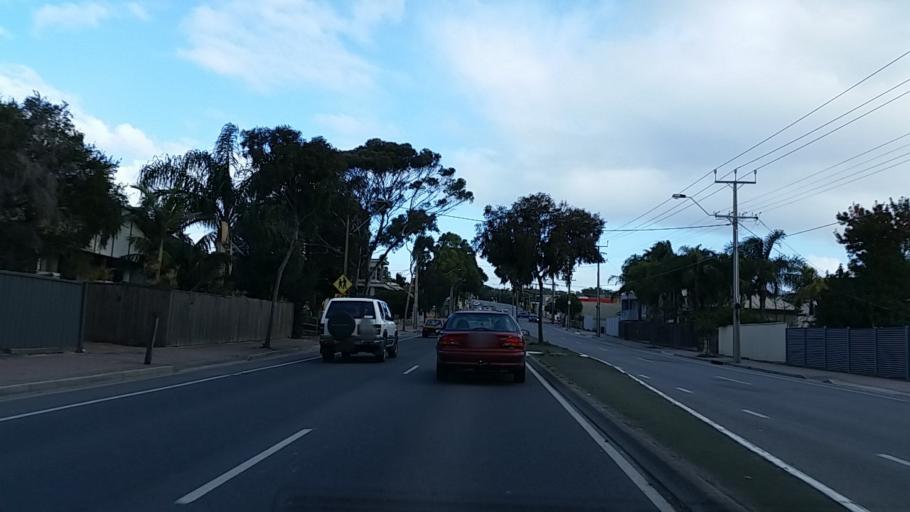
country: AU
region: South Australia
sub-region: Adelaide Hills
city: Seacliff
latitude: -35.0344
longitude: 138.5243
